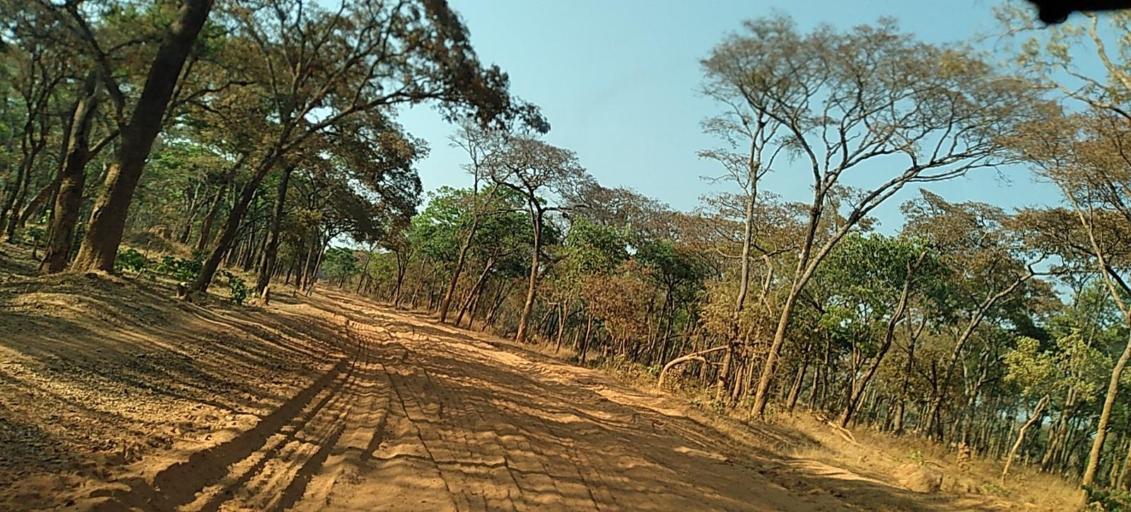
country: ZM
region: North-Western
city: Kasempa
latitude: -13.6055
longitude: 25.9773
